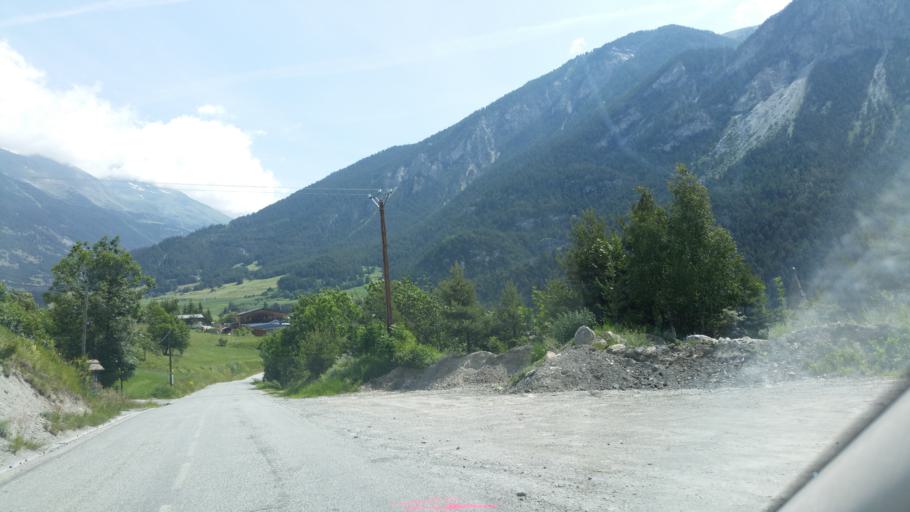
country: FR
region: Rhone-Alpes
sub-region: Departement de la Savoie
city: Modane
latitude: 45.2639
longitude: 6.8050
